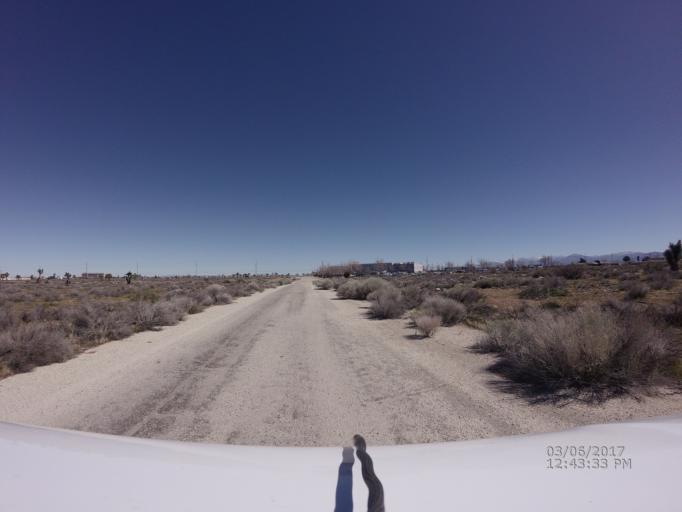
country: US
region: California
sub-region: Los Angeles County
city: Desert View Highlands
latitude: 34.6386
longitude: -118.1510
